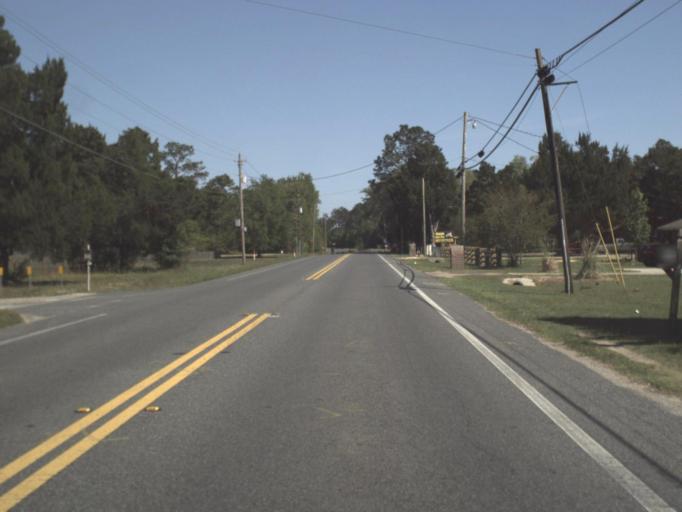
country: US
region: Florida
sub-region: Escambia County
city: Bellview
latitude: 30.5038
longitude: -87.3511
